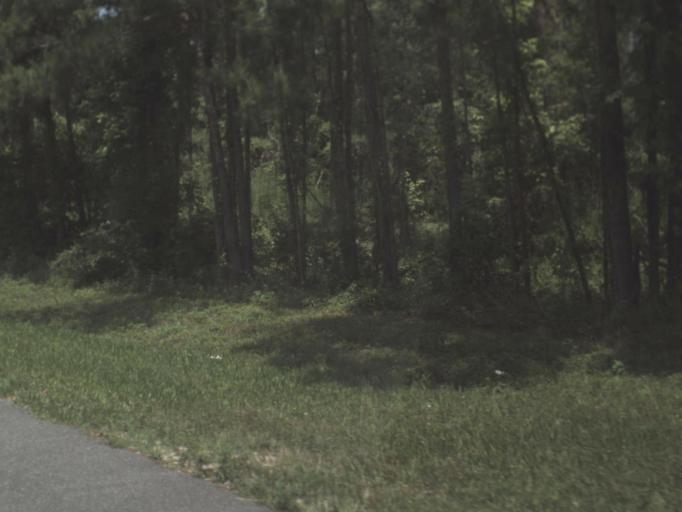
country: US
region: Florida
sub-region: Levy County
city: Williston
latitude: 29.4479
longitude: -82.4109
